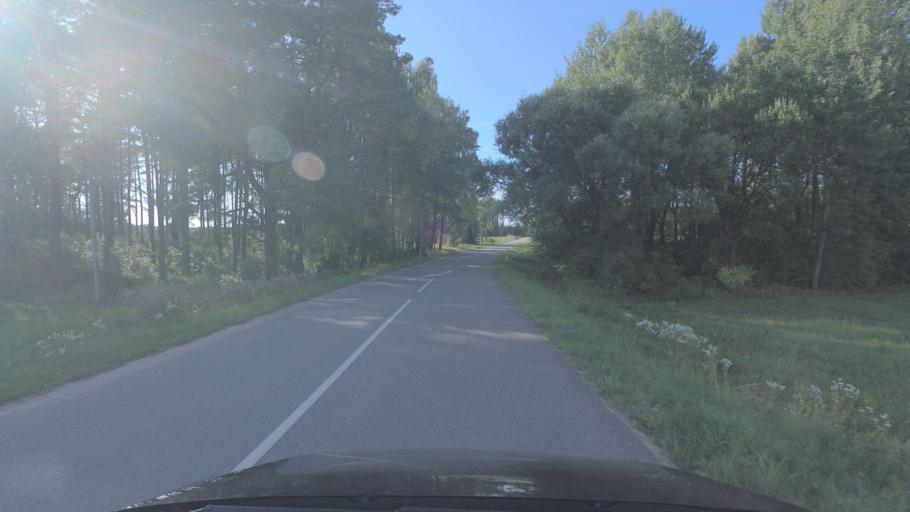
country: LT
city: Pabrade
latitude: 55.0939
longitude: 25.6834
